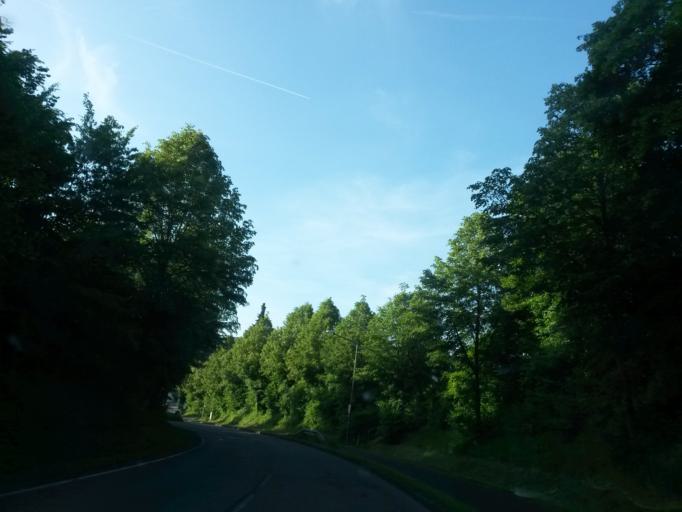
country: DE
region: North Rhine-Westphalia
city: Bergneustadt
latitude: 51.0173
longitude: 7.6554
